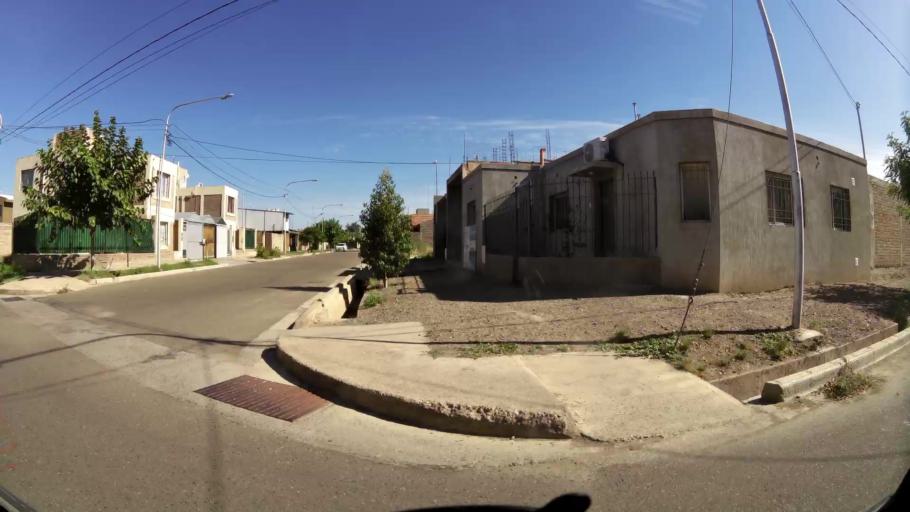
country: AR
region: Mendoza
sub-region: Departamento de Godoy Cruz
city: Godoy Cruz
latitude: -32.9454
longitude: -68.8123
